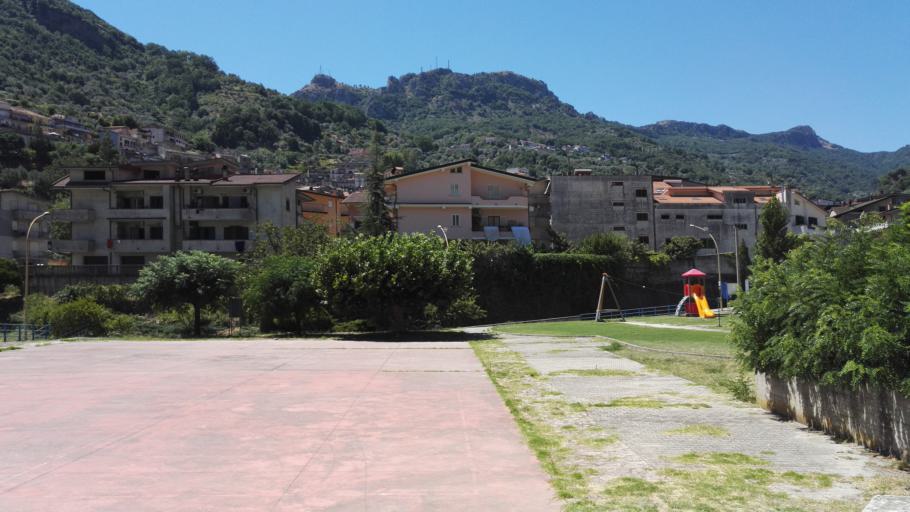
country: IT
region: Calabria
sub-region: Provincia di Reggio Calabria
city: Bivongi
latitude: 38.4864
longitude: 16.4542
